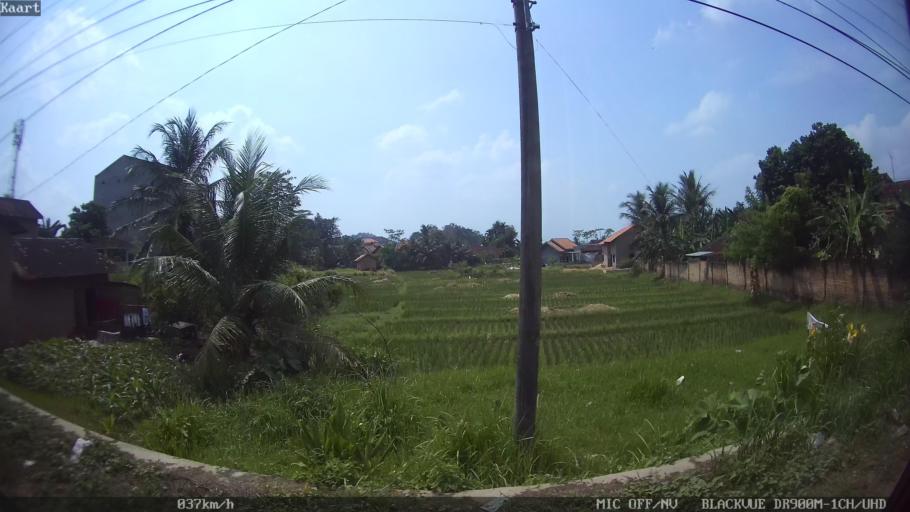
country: ID
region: Lampung
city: Pringsewu
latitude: -5.3684
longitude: 104.9677
